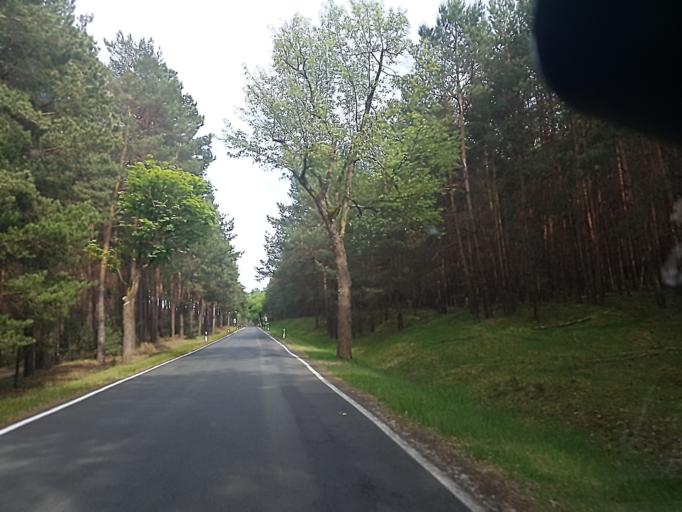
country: DE
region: Brandenburg
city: Belzig
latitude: 52.0714
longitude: 12.5438
